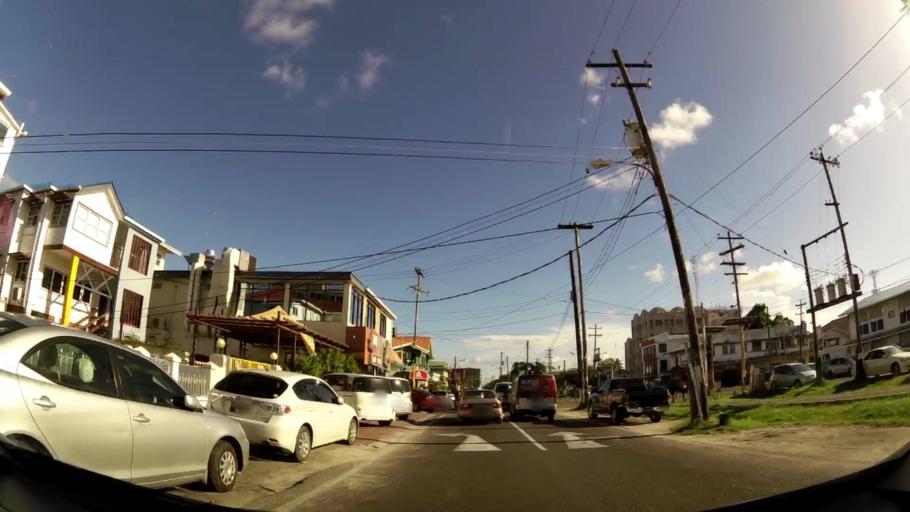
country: GY
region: Demerara-Mahaica
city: Georgetown
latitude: 6.8157
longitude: -58.1592
